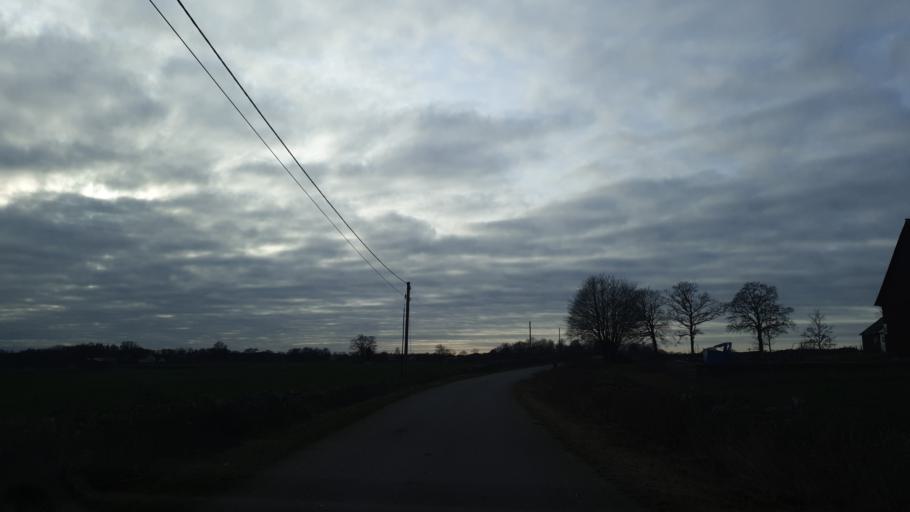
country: SE
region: Kalmar
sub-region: Torsas Kommun
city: Torsas
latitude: 56.3305
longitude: 16.0459
